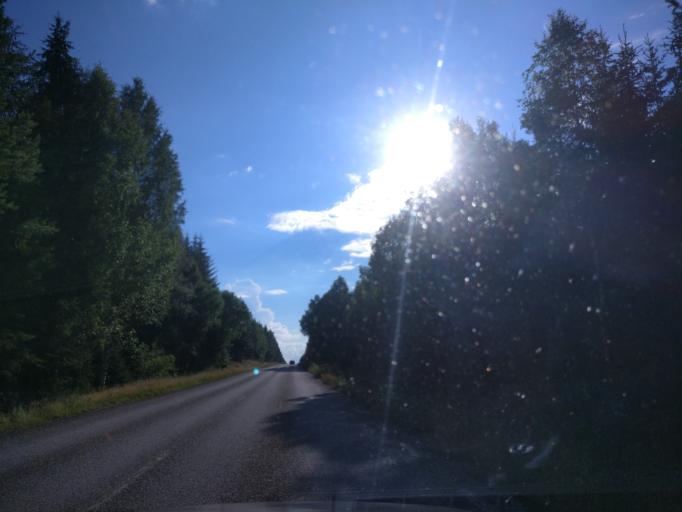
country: SE
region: Dalarna
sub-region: Ludvika Kommun
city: Ludvika
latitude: 60.2939
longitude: 15.2063
